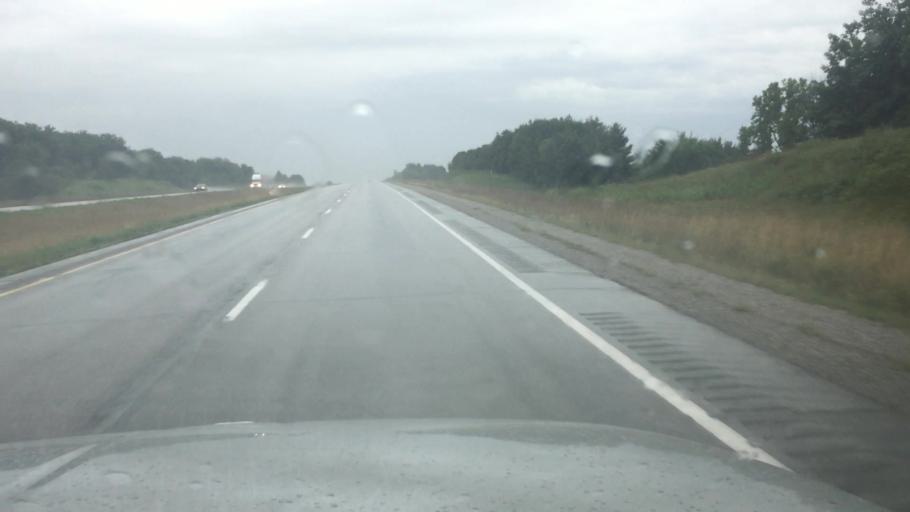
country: US
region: Iowa
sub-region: Johnson County
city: Lone Tree
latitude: 41.4214
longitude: -91.5513
